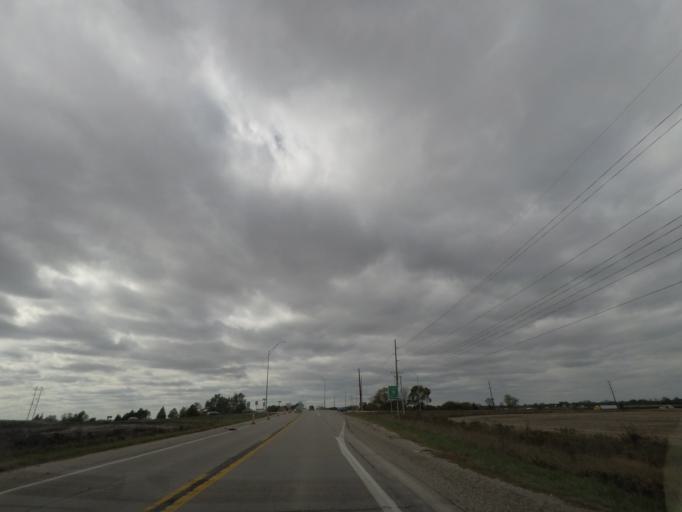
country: US
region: Iowa
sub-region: Story County
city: Huxley
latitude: 41.8778
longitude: -93.5673
